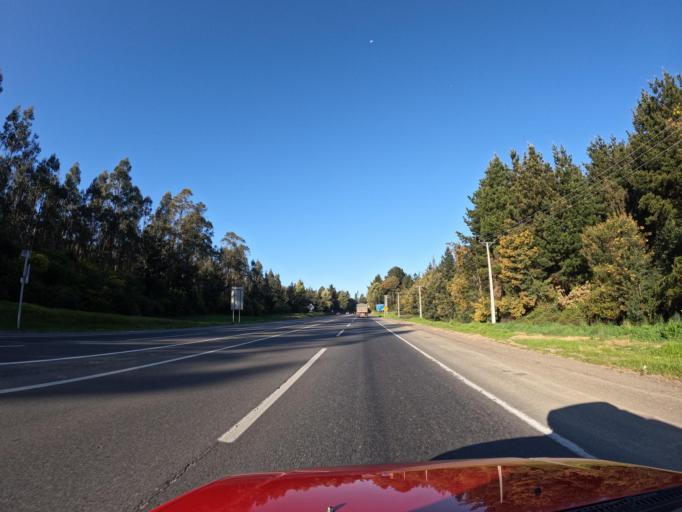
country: CL
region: Biobio
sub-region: Provincia de Concepcion
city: Penco
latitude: -36.7606
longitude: -72.9677
